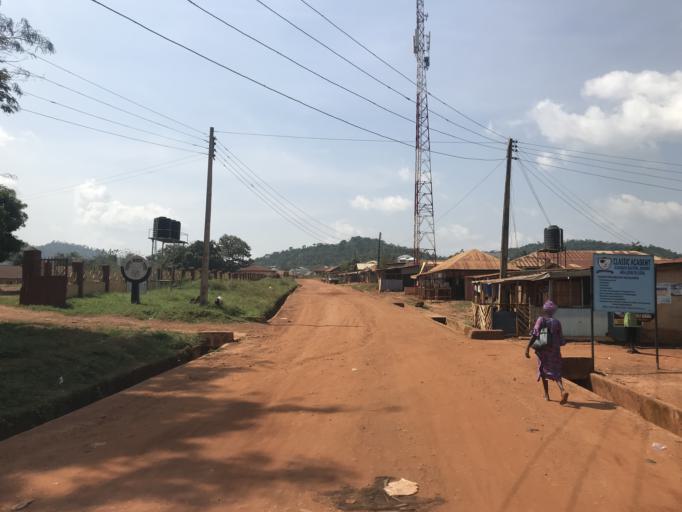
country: NG
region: Osun
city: Ilesa
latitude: 7.6209
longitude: 4.7103
